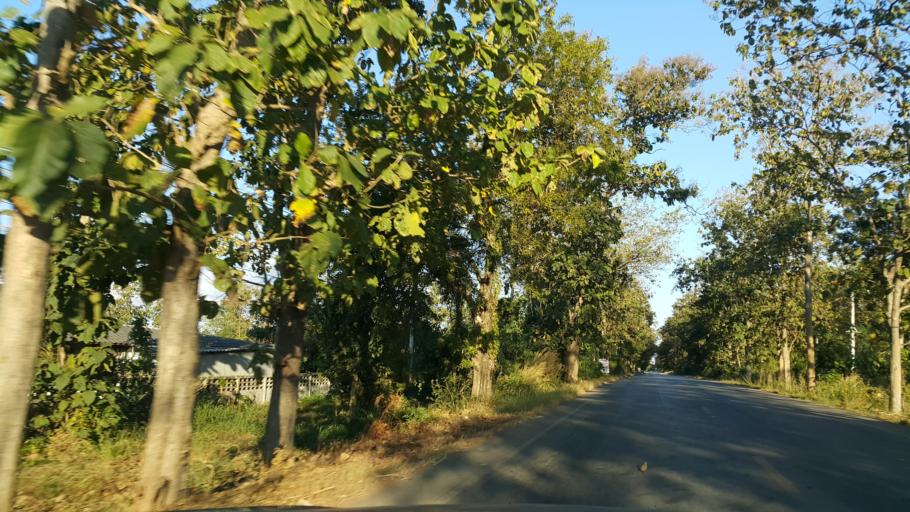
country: TH
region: Sukhothai
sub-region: Amphoe Si Satchanalai
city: Si Satchanalai
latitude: 17.5385
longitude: 99.8074
